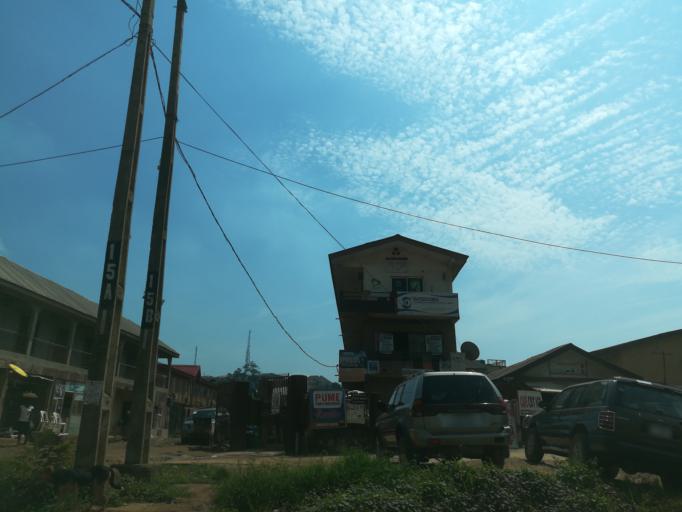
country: NG
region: Lagos
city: Ikorodu
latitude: 6.6459
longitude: 3.4795
